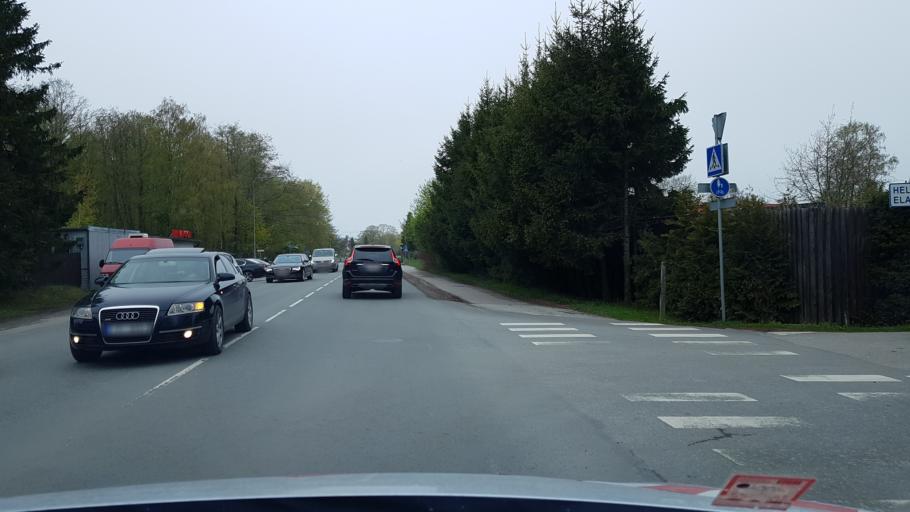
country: EE
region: Harju
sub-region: Viimsi vald
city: Haabneeme
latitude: 59.5155
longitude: 24.8166
